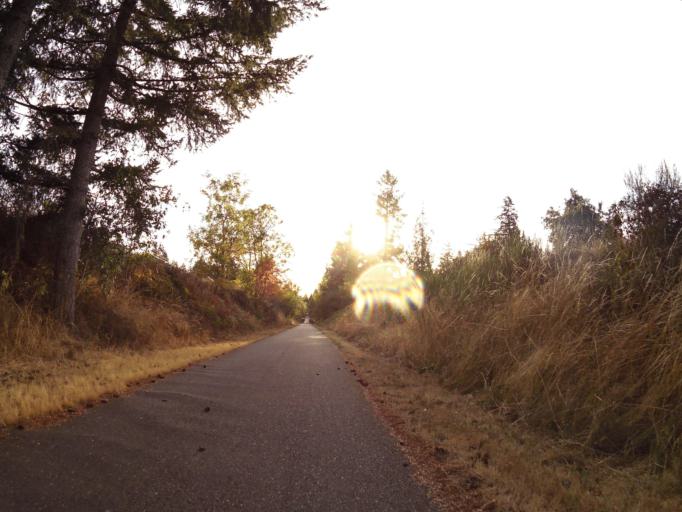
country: US
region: Washington
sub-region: Thurston County
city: Rainier
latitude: 46.8735
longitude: -122.7285
